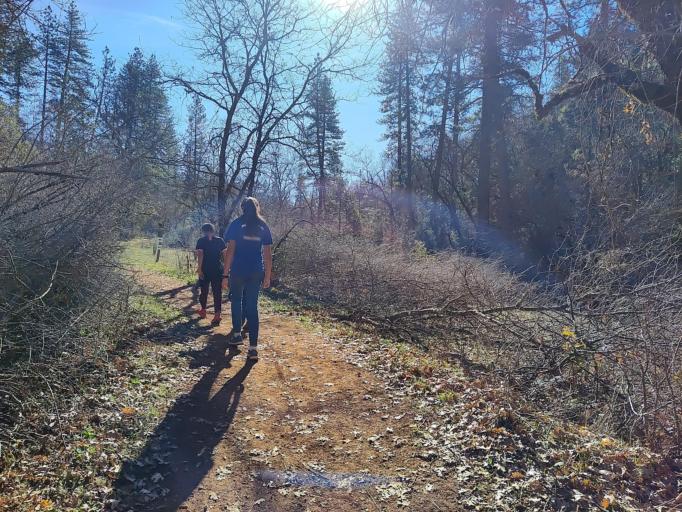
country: US
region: California
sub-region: Placer County
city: Meadow Vista
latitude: 39.0249
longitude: -120.9882
